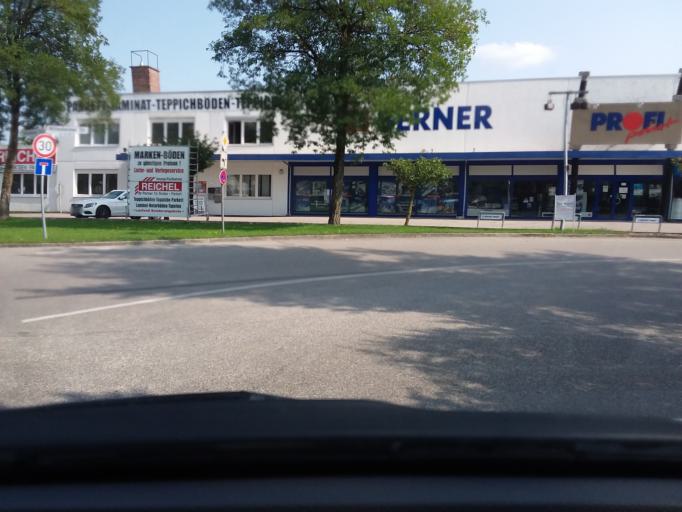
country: DE
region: Bavaria
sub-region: Upper Bavaria
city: Oberschleissheim
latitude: 48.2637
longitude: 11.5573
